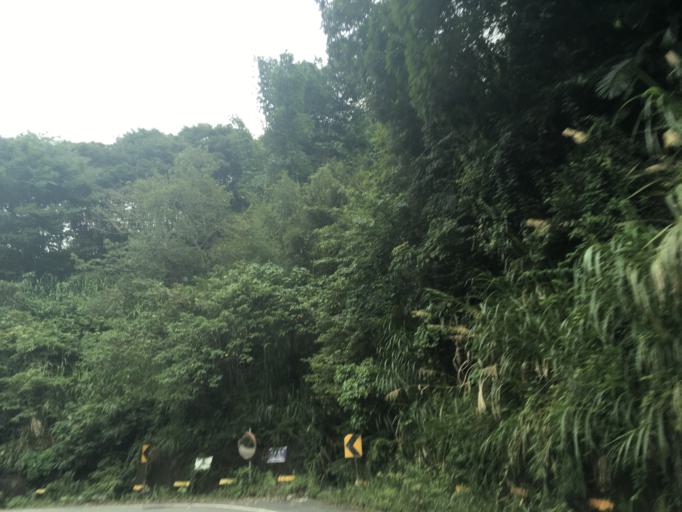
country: TW
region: Taiwan
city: Fengyuan
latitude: 24.3350
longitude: 120.9266
